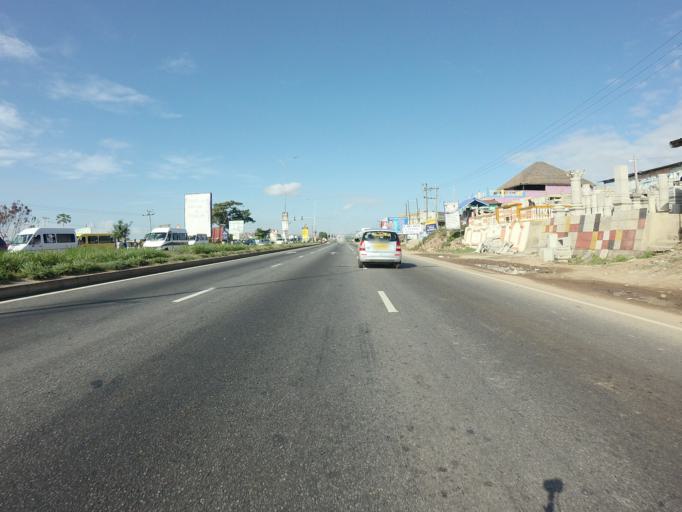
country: GH
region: Greater Accra
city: Gbawe
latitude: 5.5565
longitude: -0.3019
